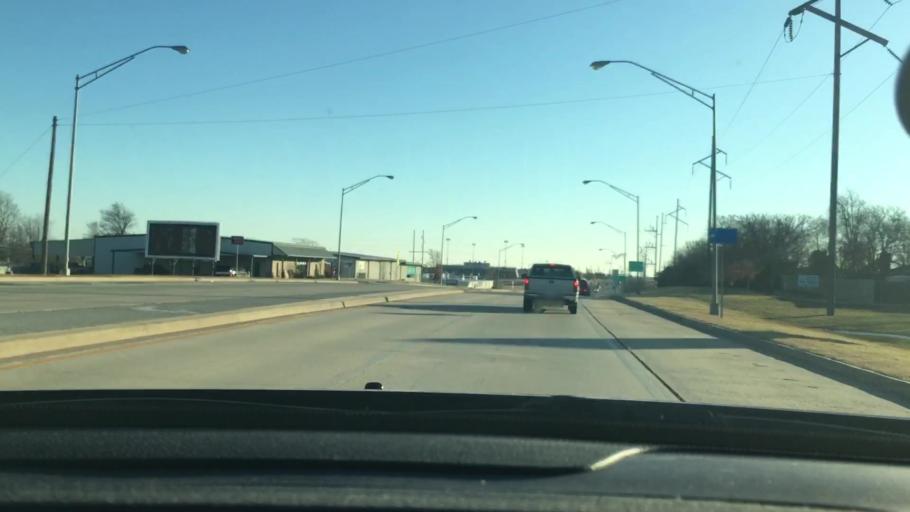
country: US
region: Oklahoma
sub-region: Carter County
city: Ardmore
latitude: 34.2028
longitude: -97.1468
